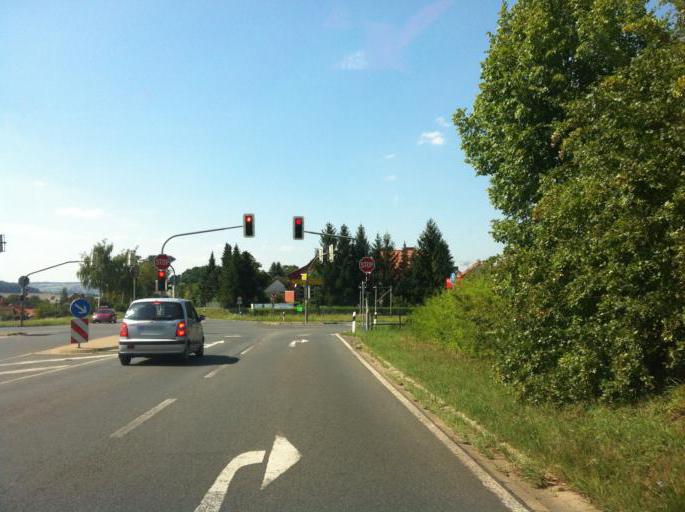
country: DE
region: Lower Saxony
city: Rosdorf
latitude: 51.4745
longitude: 9.9424
